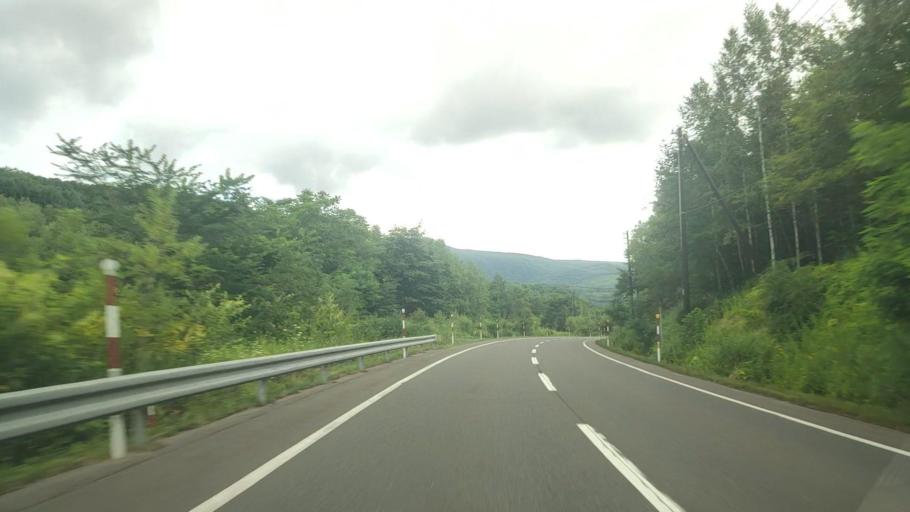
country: JP
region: Hokkaido
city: Date
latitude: 42.5976
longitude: 141.0282
